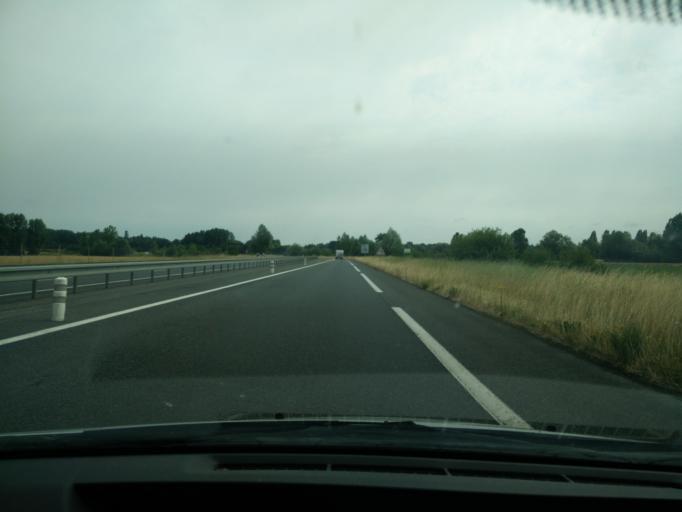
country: FR
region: Pays de la Loire
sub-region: Departement de Maine-et-Loire
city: Doue-la-Fontaine
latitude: 47.2093
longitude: -0.3087
